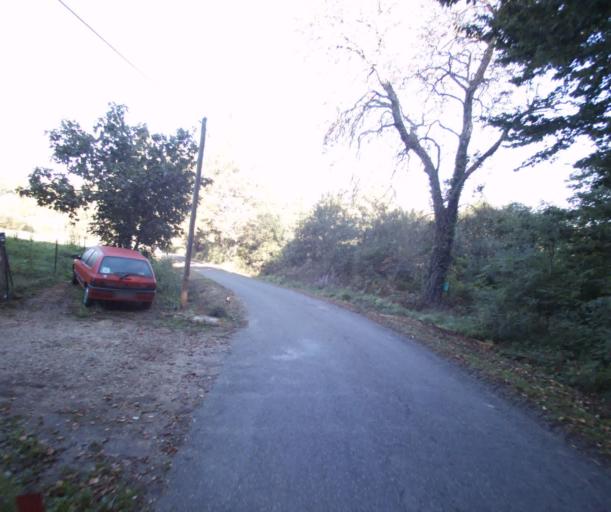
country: FR
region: Midi-Pyrenees
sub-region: Departement du Gers
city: Cazaubon
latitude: 43.9098
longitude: -0.0066
